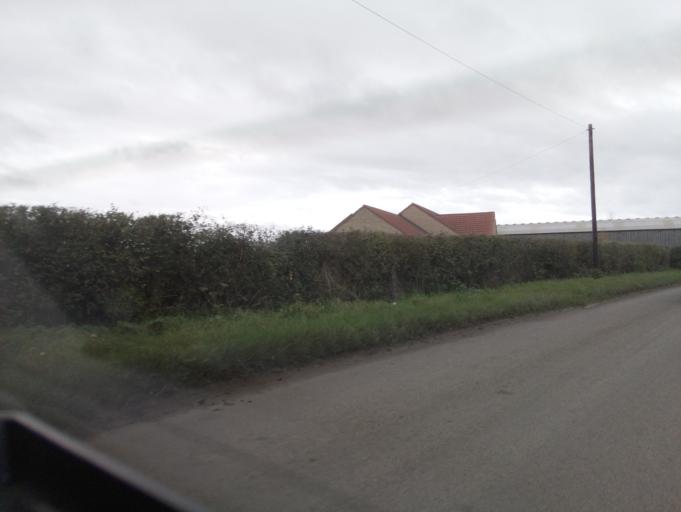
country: GB
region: England
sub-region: Somerset
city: Yeovil
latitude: 51.0019
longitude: -2.5909
